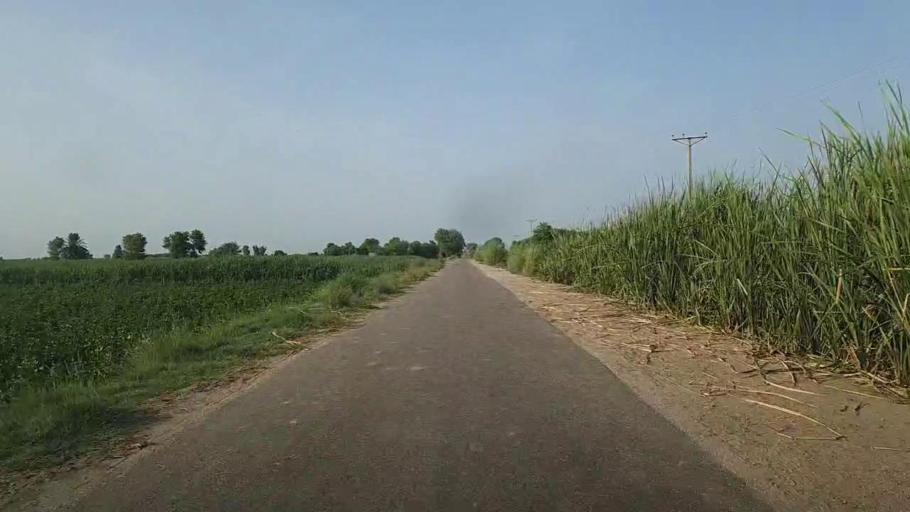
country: PK
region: Sindh
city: Ubauro
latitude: 28.0943
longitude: 69.8210
